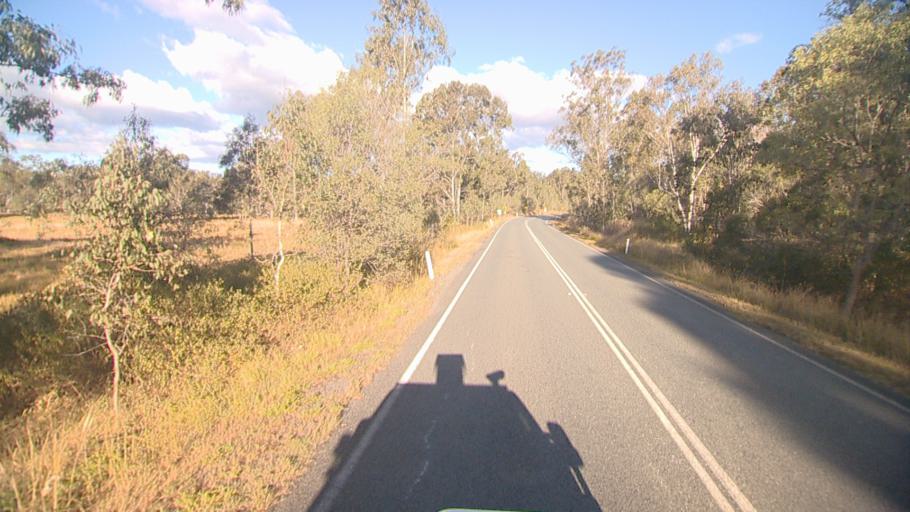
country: AU
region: Queensland
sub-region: Logan
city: Cedar Vale
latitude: -27.8928
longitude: 153.0866
